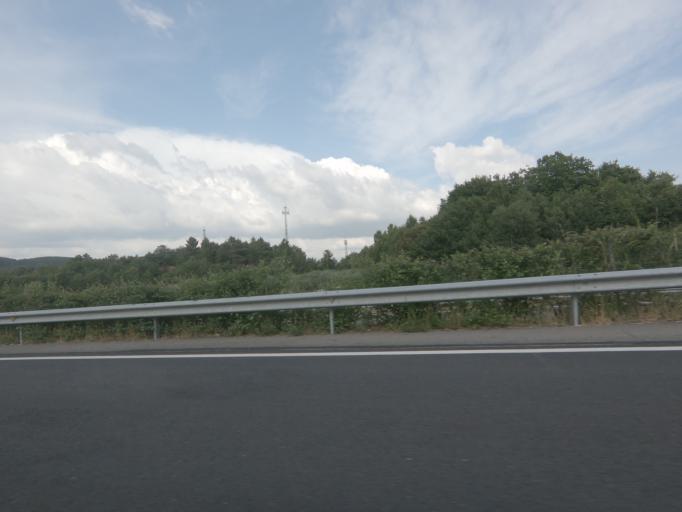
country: ES
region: Galicia
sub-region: Provincia de Ourense
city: Ambia
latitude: 42.1641
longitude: -7.7606
